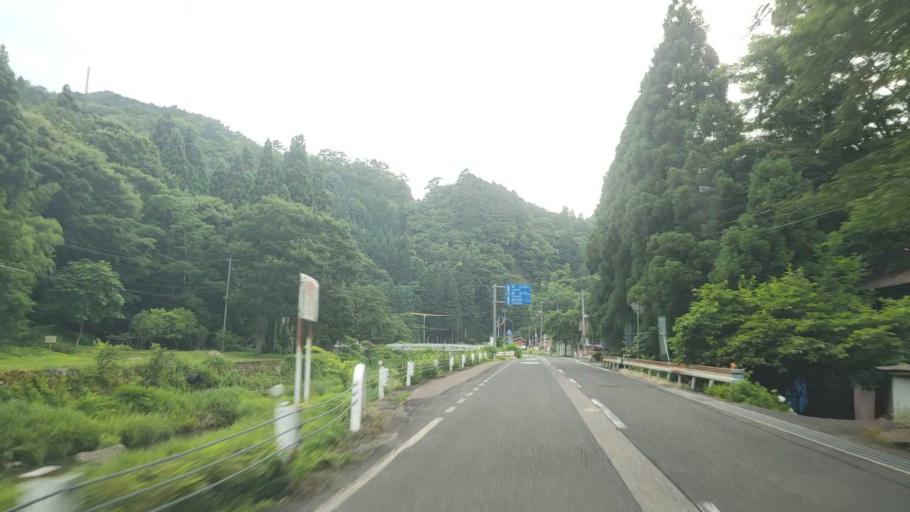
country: JP
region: Tottori
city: Tottori
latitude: 35.3299
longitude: 134.0559
